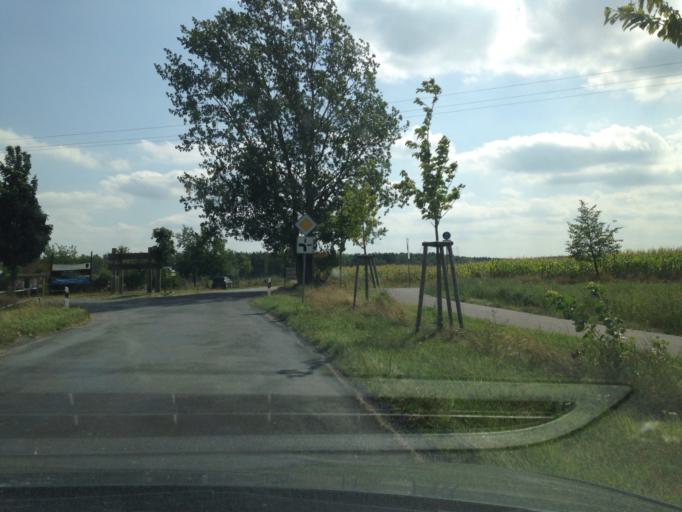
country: DE
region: Brandenburg
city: Lychen
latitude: 53.2997
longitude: 13.4268
